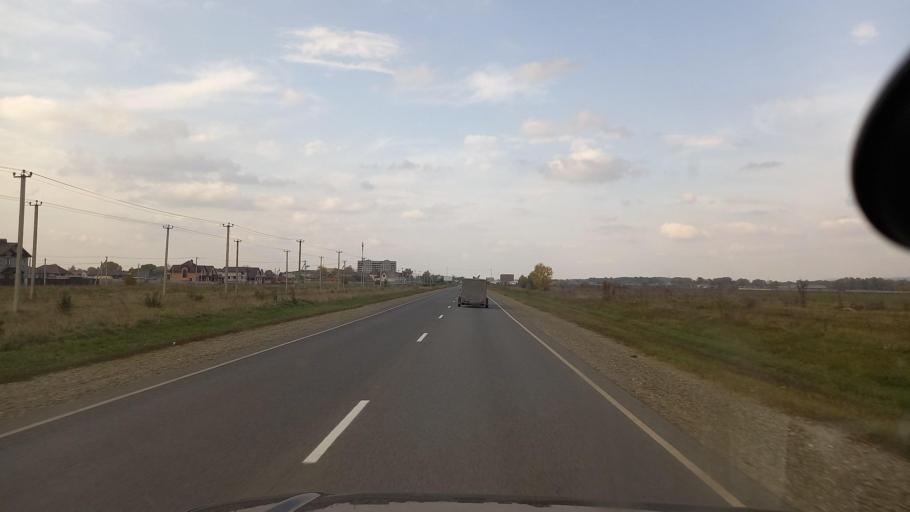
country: RU
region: Krasnodarskiy
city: Mostovskoy
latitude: 44.3850
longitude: 40.8190
